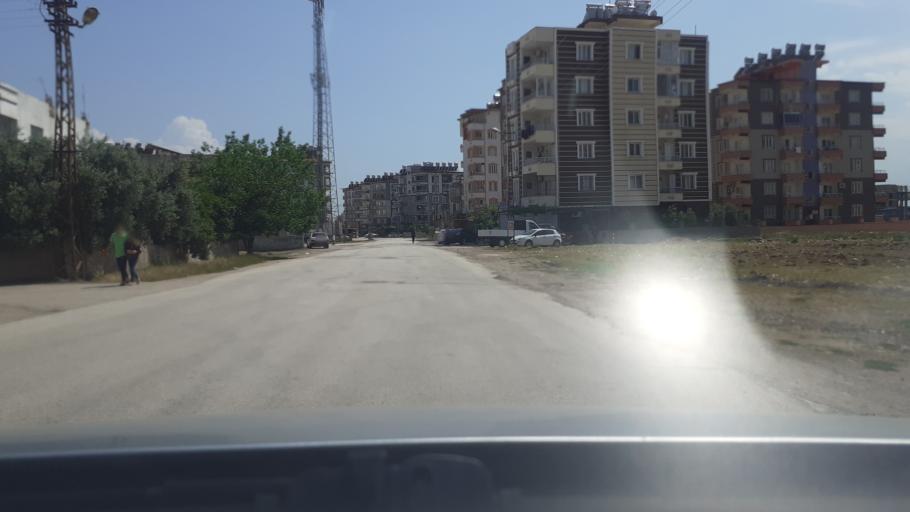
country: TR
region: Hatay
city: Kirikhan
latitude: 36.4832
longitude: 36.3555
